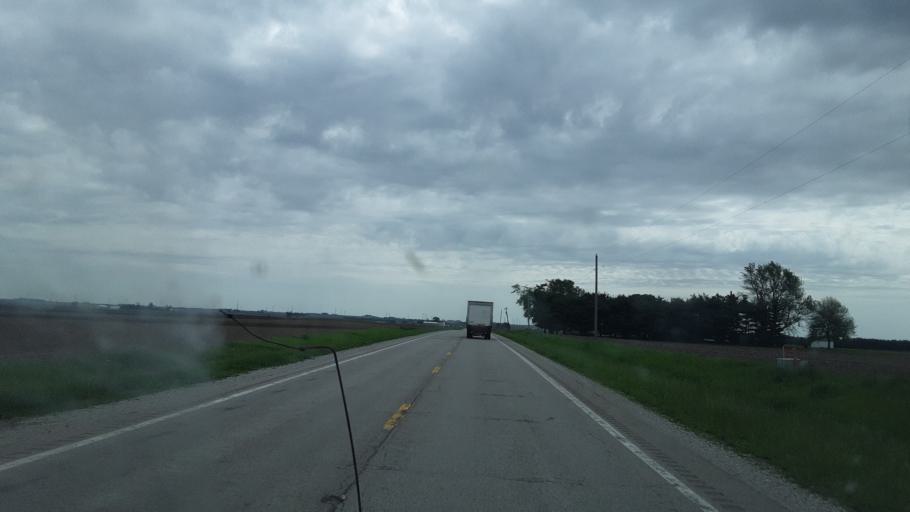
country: US
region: Illinois
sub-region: Tazewell County
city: Delavan
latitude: 40.3068
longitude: -89.5178
